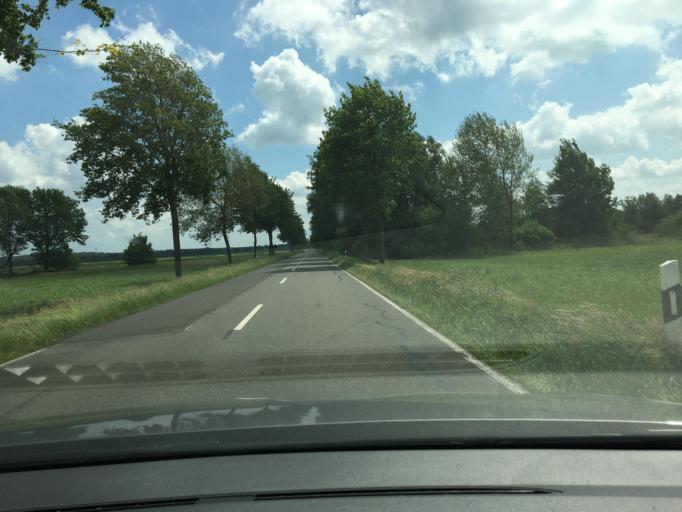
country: DE
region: Lower Saxony
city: Tarmstedt
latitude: 53.2388
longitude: 9.0349
